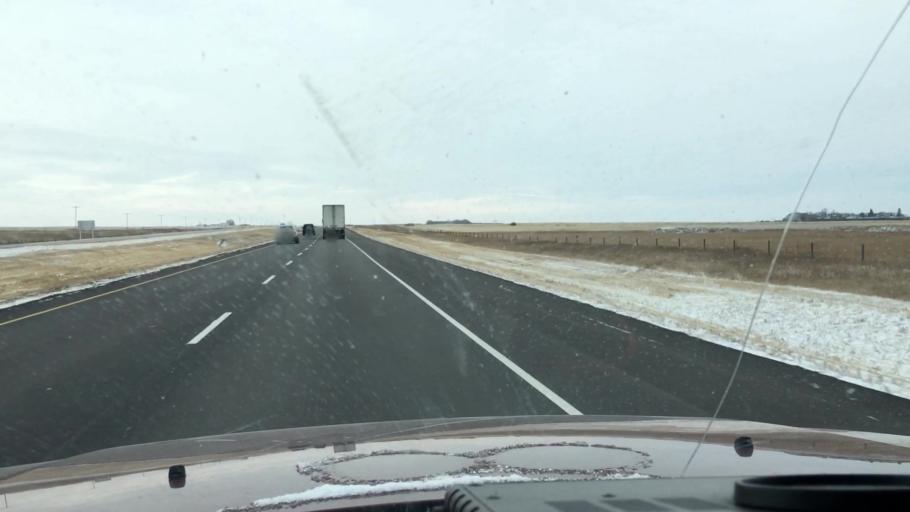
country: CA
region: Saskatchewan
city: Saskatoon
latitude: 51.8023
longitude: -106.4909
